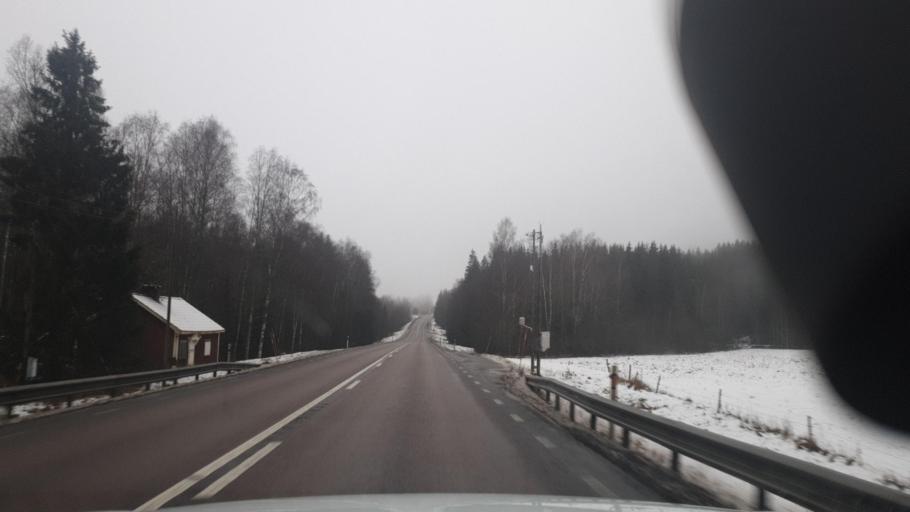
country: SE
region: Vaermland
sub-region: Sunne Kommun
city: Sunne
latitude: 59.6675
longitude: 12.9024
